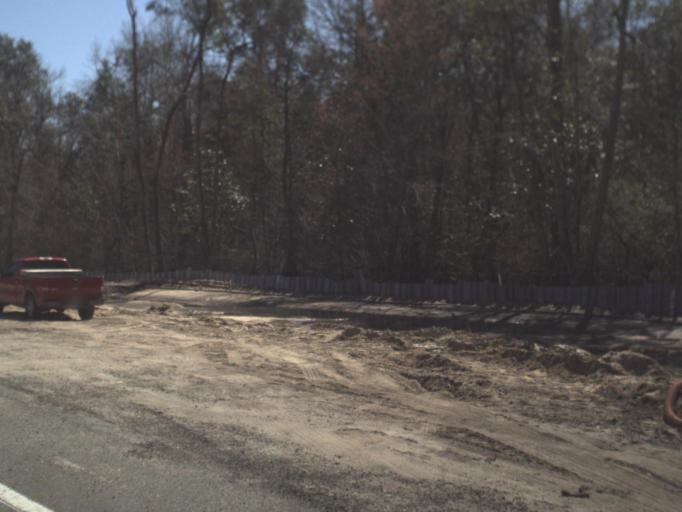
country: US
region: Florida
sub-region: Leon County
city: Tallahassee
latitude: 30.4487
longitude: -84.3570
